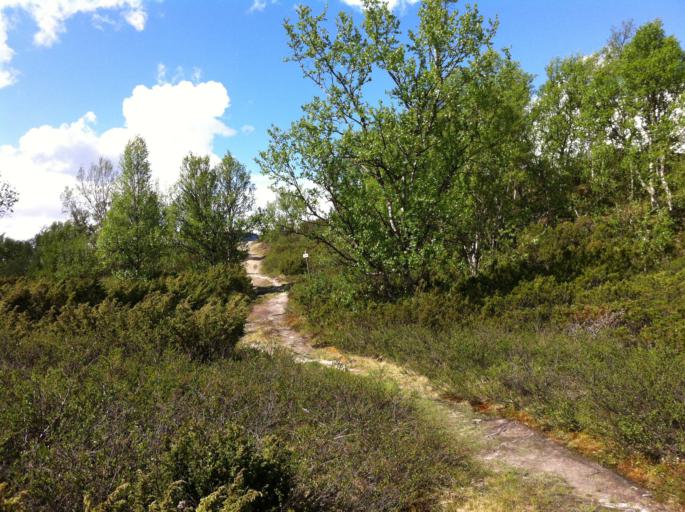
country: SE
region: Jaemtland
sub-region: Are Kommun
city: Are
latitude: 62.7094
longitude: 12.4991
